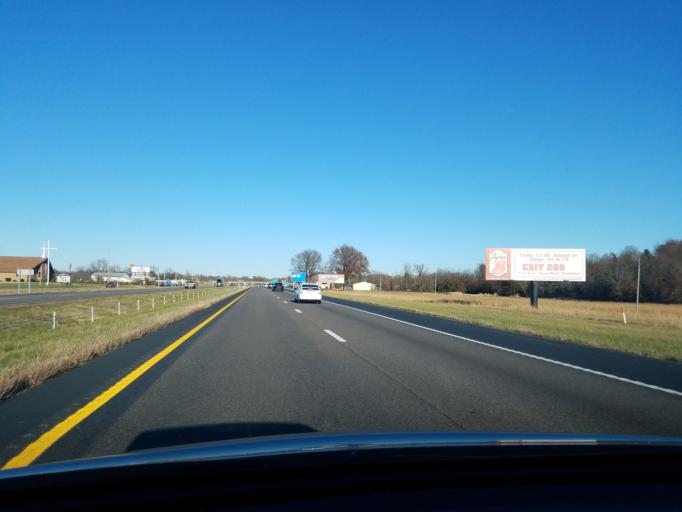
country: US
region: Missouri
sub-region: Phelps County
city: Saint James
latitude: 38.0002
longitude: -91.6257
